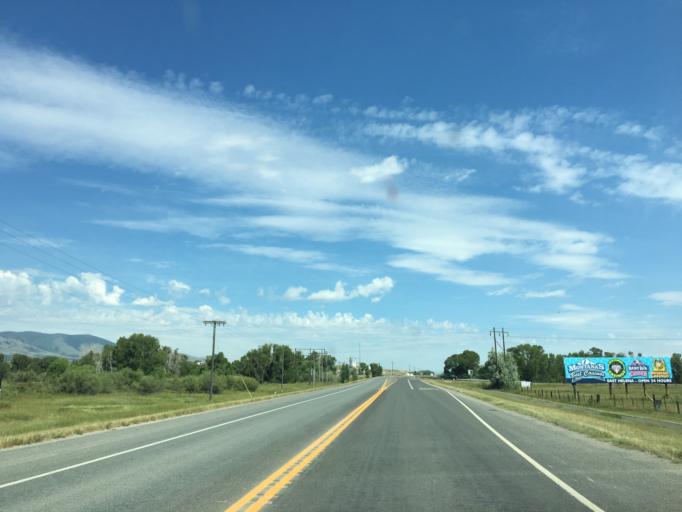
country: US
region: Montana
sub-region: Broadwater County
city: Townsend
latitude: 46.3305
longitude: -111.5290
